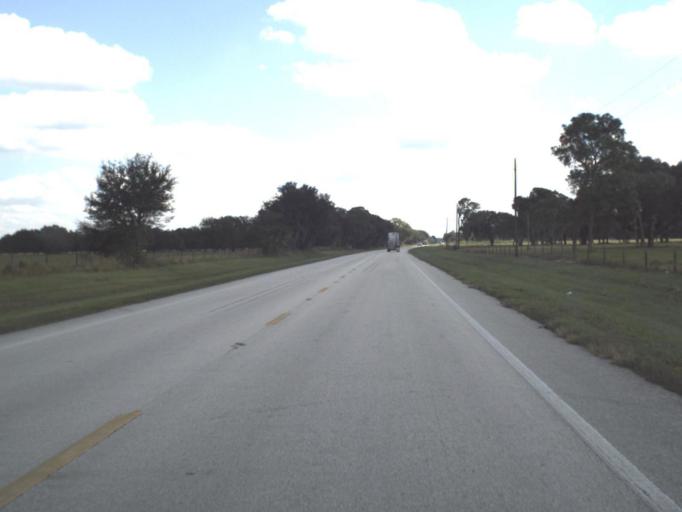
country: US
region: Florida
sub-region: Hardee County
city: Zolfo Springs
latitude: 27.4579
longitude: -81.6728
